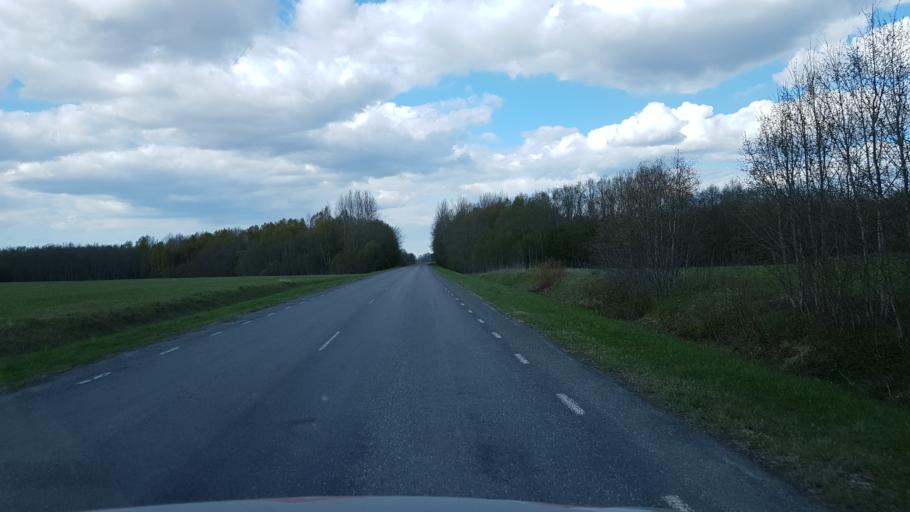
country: EE
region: Harju
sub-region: Keila linn
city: Keila
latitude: 59.2658
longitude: 24.4533
